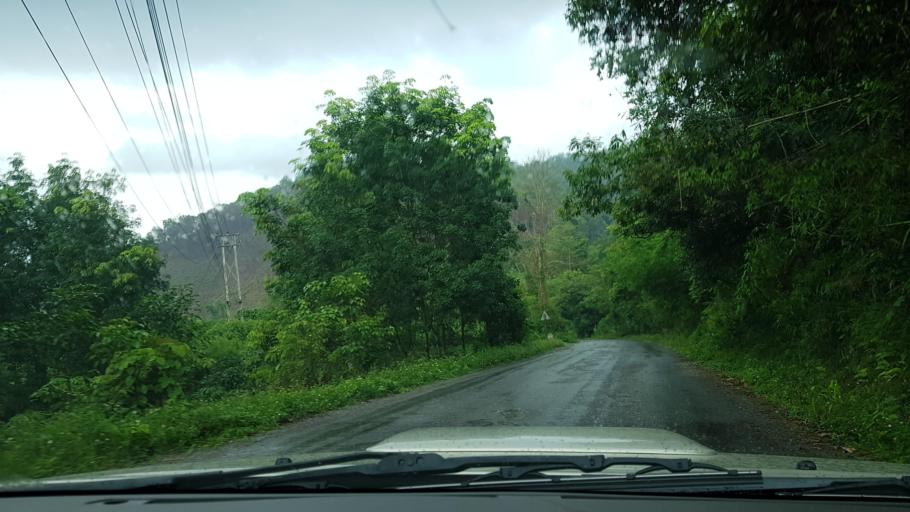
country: LA
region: Oudomxai
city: Muang Xay
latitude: 20.6063
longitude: 101.9447
